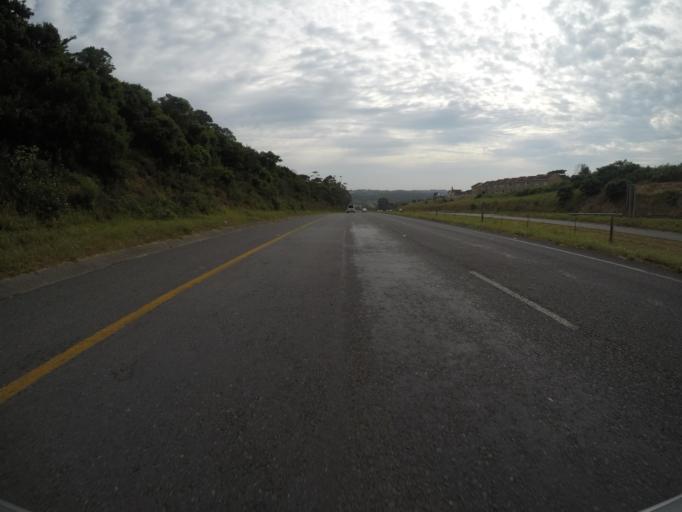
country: ZA
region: Eastern Cape
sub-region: Buffalo City Metropolitan Municipality
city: East London
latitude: -32.9499
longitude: 27.9342
